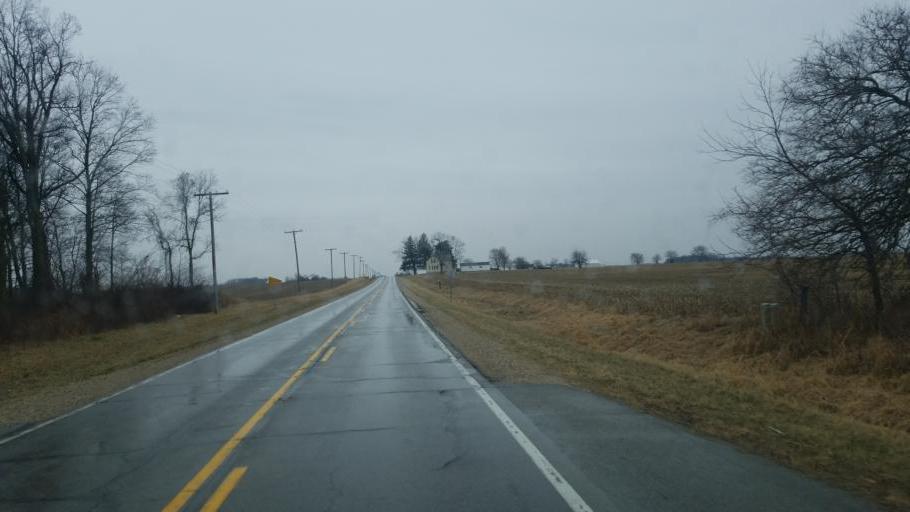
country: US
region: Indiana
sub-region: Adams County
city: Berne
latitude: 40.6344
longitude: -85.0413
